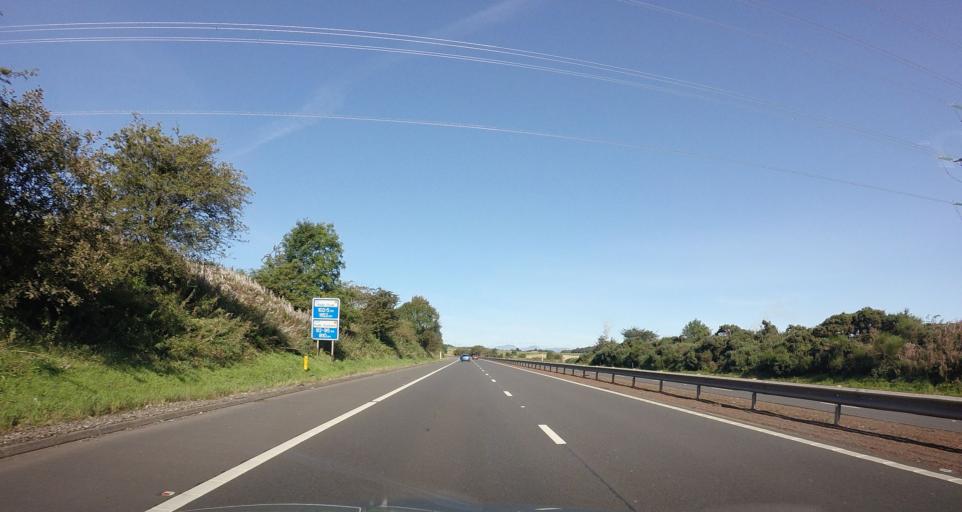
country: GB
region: Scotland
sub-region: Stirling
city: Cowie
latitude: 56.0601
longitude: -3.8564
